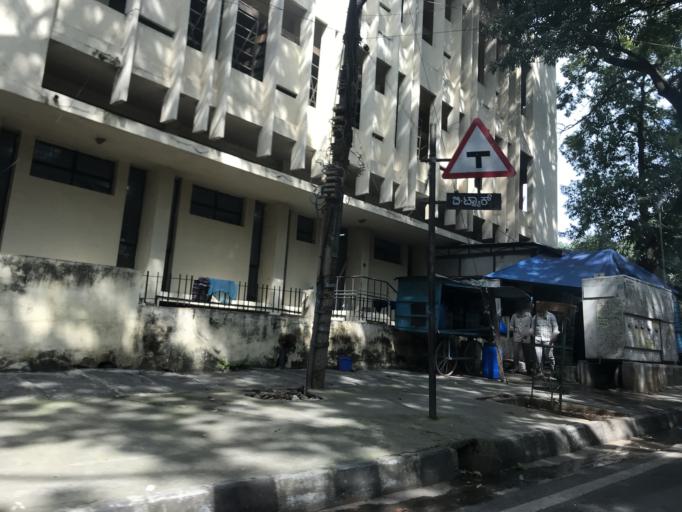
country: IN
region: Karnataka
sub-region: Bangalore Urban
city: Bangalore
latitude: 12.9581
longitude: 77.5713
